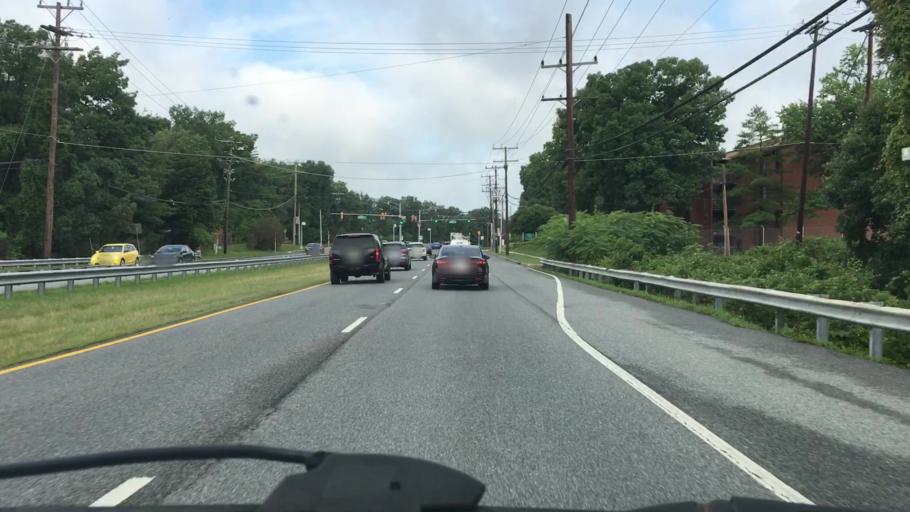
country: US
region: Maryland
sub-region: Prince George's County
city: Goddard
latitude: 38.9916
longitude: -76.8623
